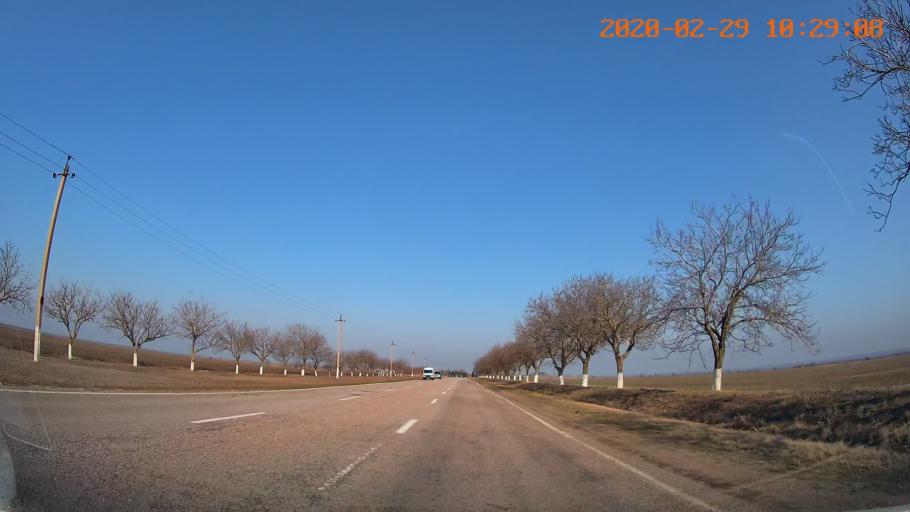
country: MD
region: Telenesti
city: Tiraspolul Nou
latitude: 46.9198
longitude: 29.5874
